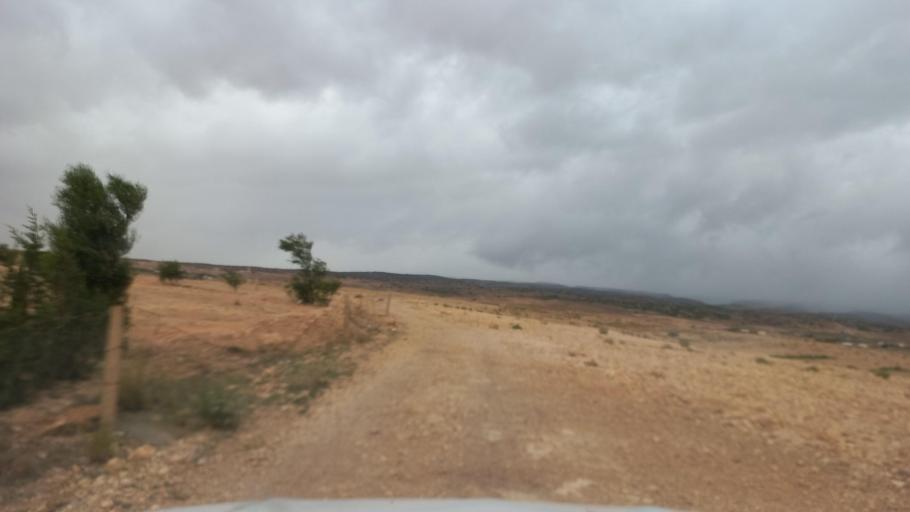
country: TN
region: Al Qasrayn
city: Kasserine
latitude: 35.2780
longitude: 8.9368
